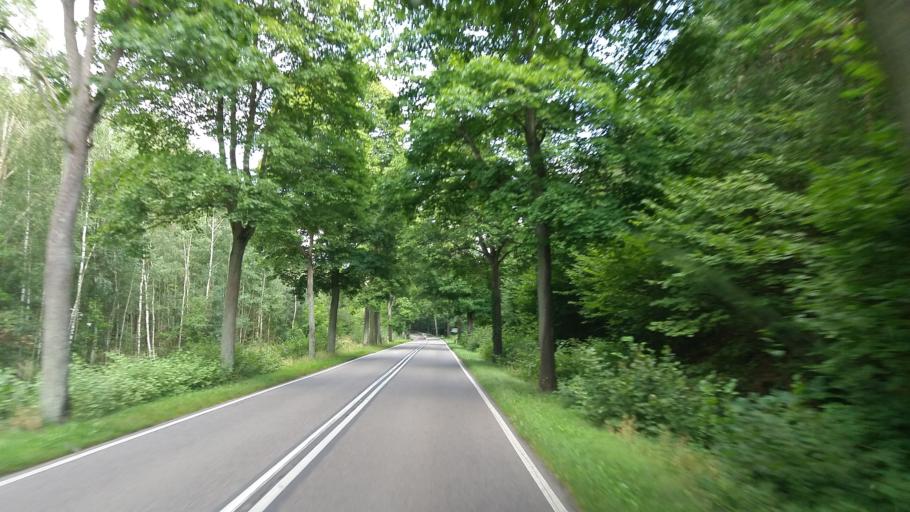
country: PL
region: West Pomeranian Voivodeship
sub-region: Powiat mysliborski
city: Barlinek
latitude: 53.0031
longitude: 15.2314
